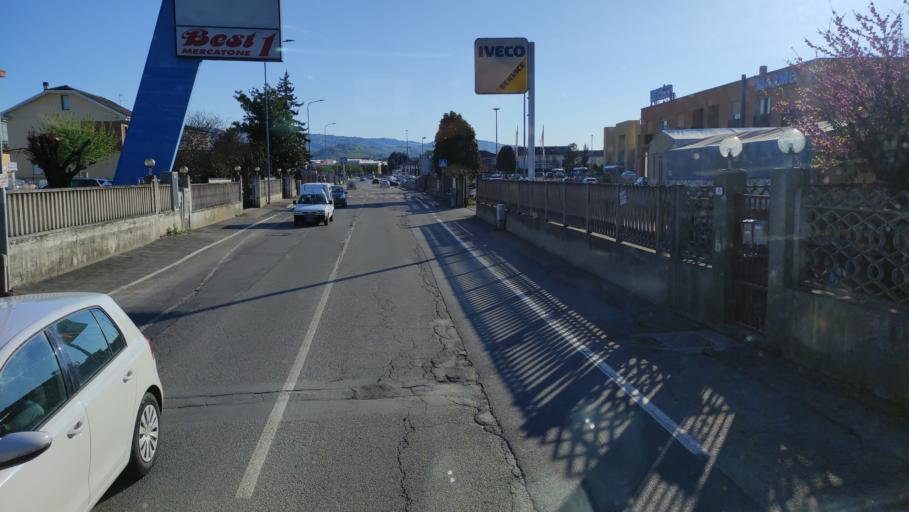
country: IT
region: Piedmont
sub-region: Provincia di Asti
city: Canelli
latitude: 44.7266
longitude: 8.3047
